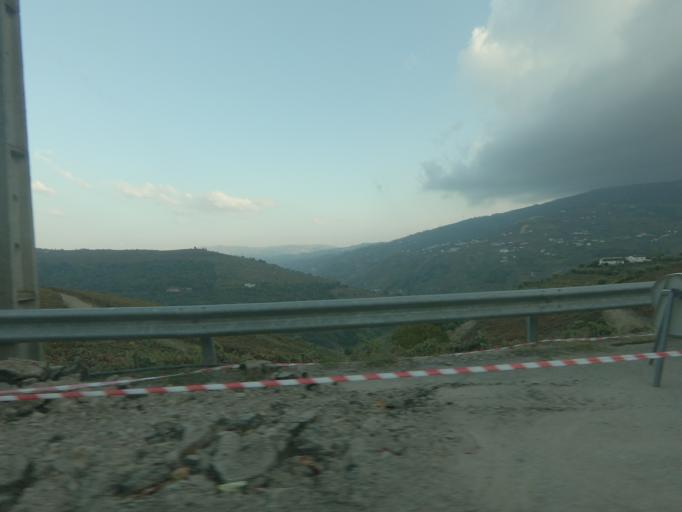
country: PT
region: Vila Real
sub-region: Mesao Frio
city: Mesao Frio
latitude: 41.1653
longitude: -7.8488
